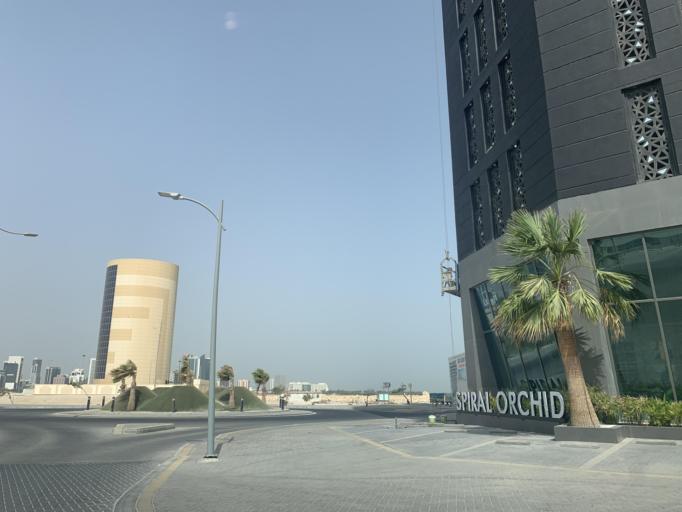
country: BH
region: Manama
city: Jidd Hafs
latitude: 26.2442
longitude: 50.5535
